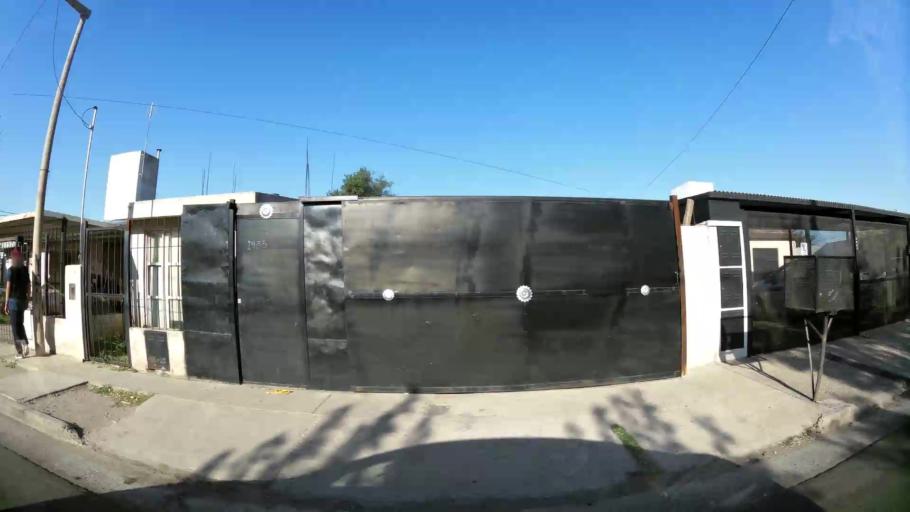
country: AR
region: Cordoba
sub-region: Departamento de Capital
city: Cordoba
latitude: -31.4426
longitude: -64.2481
